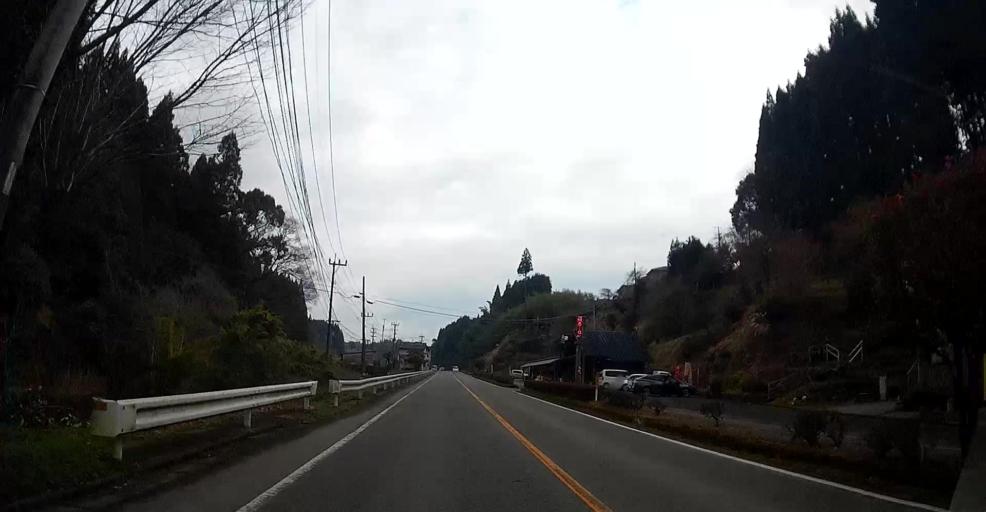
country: JP
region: Kumamoto
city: Matsubase
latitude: 32.6204
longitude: 130.8606
